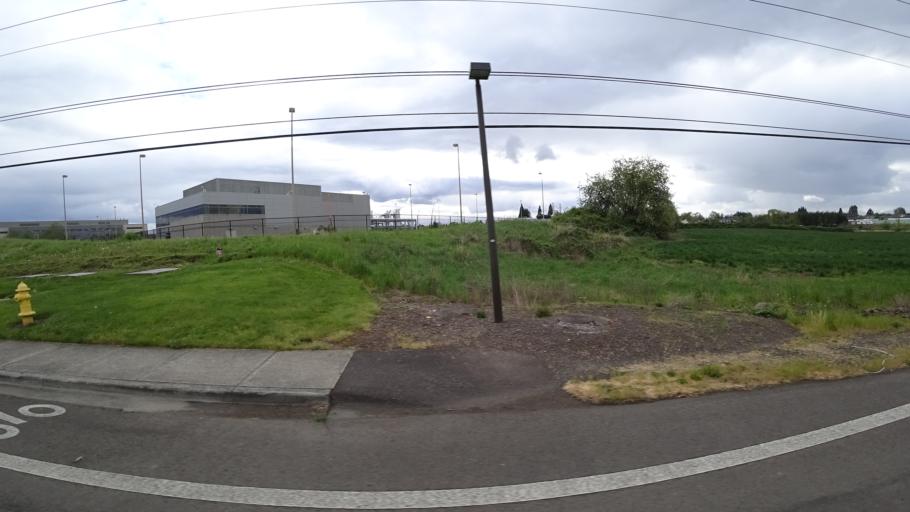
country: US
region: Oregon
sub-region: Washington County
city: Hillsboro
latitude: 45.5470
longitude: -122.9607
